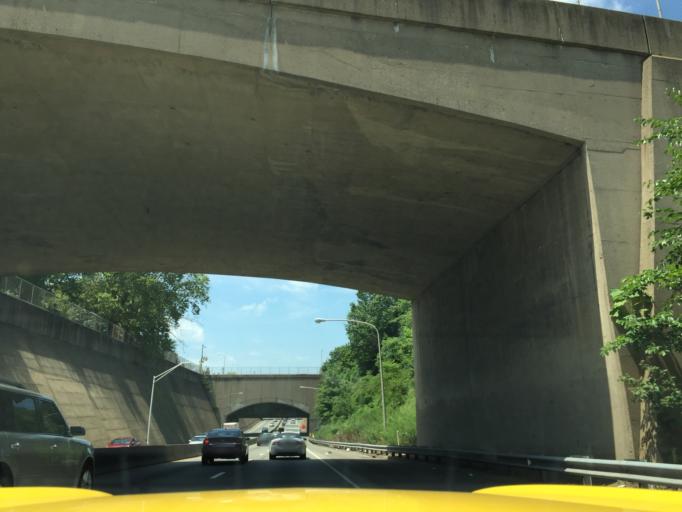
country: US
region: Pennsylvania
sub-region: Philadelphia County
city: Philadelphia
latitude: 40.0196
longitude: -75.1467
